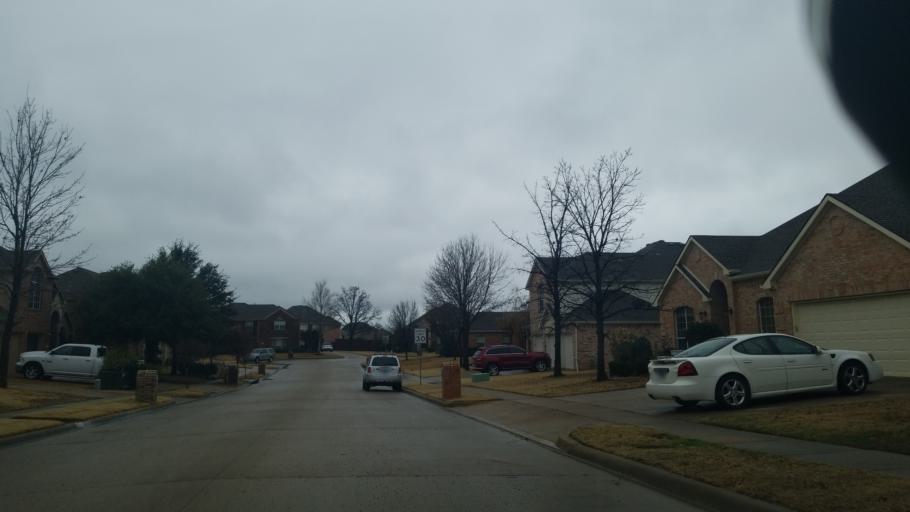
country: US
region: Texas
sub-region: Denton County
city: Corinth
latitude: 33.1420
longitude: -97.0907
